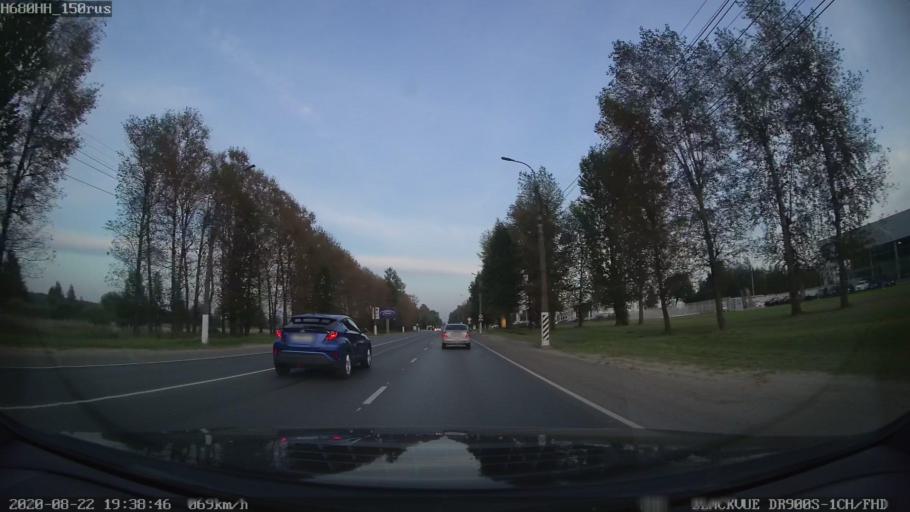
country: RU
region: Tverskaya
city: Sakharovo
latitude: 56.8107
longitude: 36.0026
